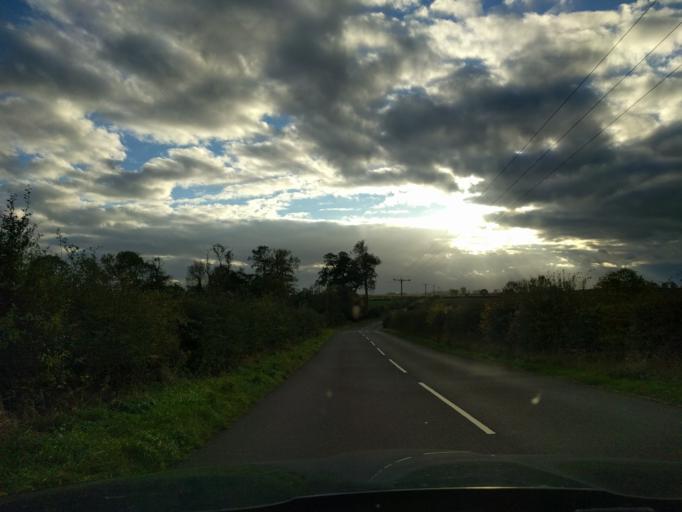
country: GB
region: England
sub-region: Northumberland
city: Ford
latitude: 55.7307
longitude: -2.1055
